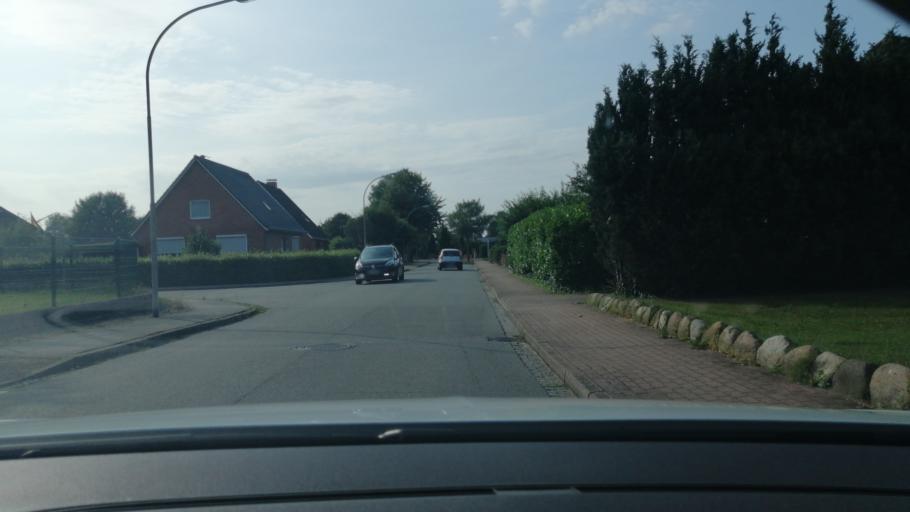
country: DE
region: Schleswig-Holstein
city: Leck
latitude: 54.7676
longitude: 8.9655
